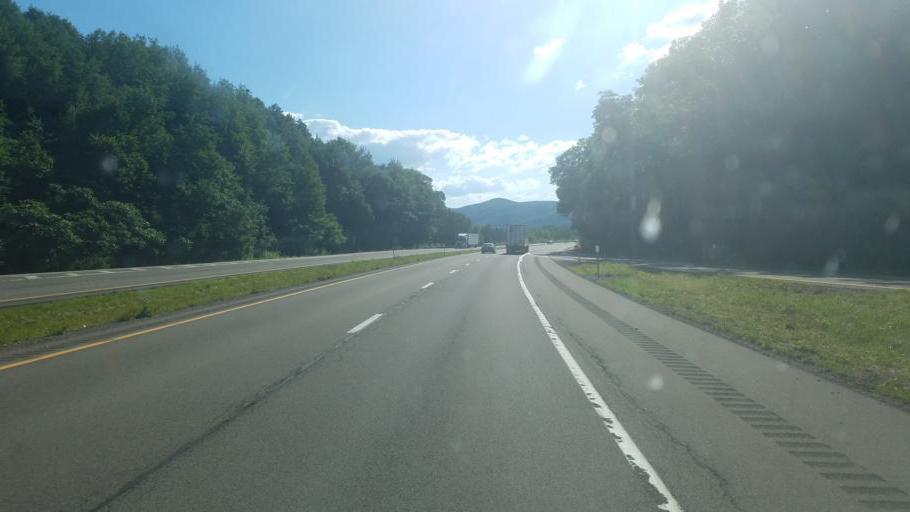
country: US
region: New York
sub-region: Cattaraugus County
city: Randolph
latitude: 42.0990
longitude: -78.8510
